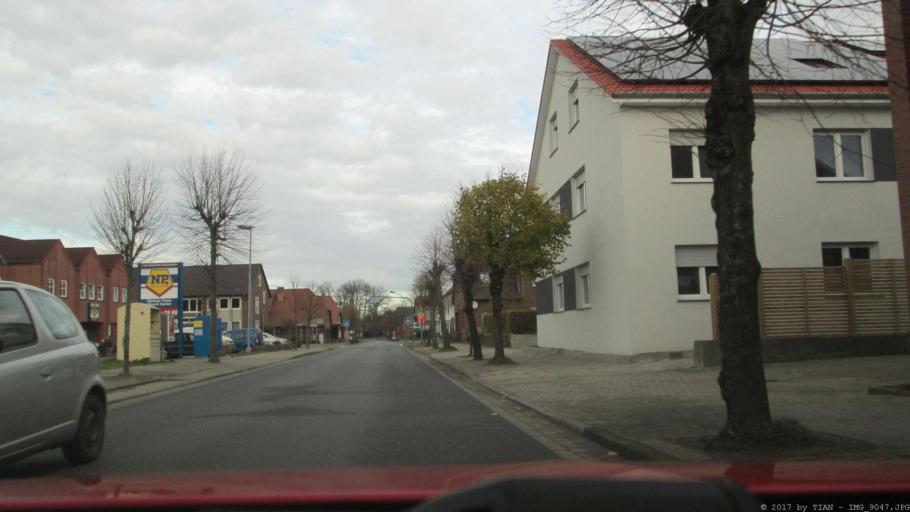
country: DE
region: Lower Saxony
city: Wittingen
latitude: 52.6783
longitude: 10.7030
